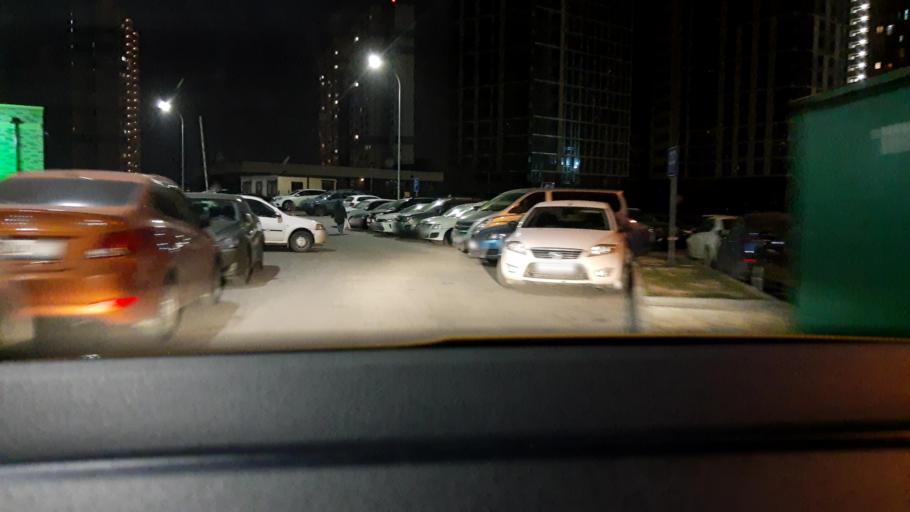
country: RU
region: Moskovskaya
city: Dolgoprudnyy
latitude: 55.9347
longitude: 37.5028
